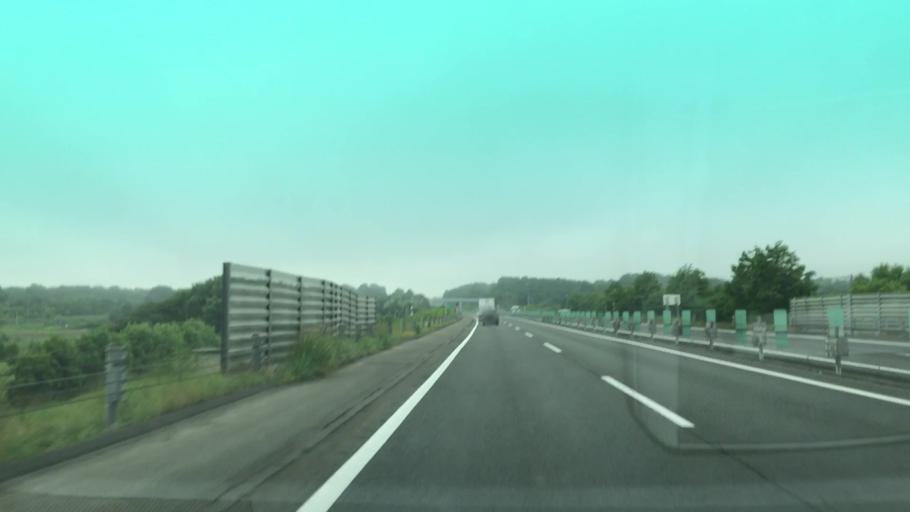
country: JP
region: Hokkaido
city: Kitahiroshima
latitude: 42.8931
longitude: 141.5496
